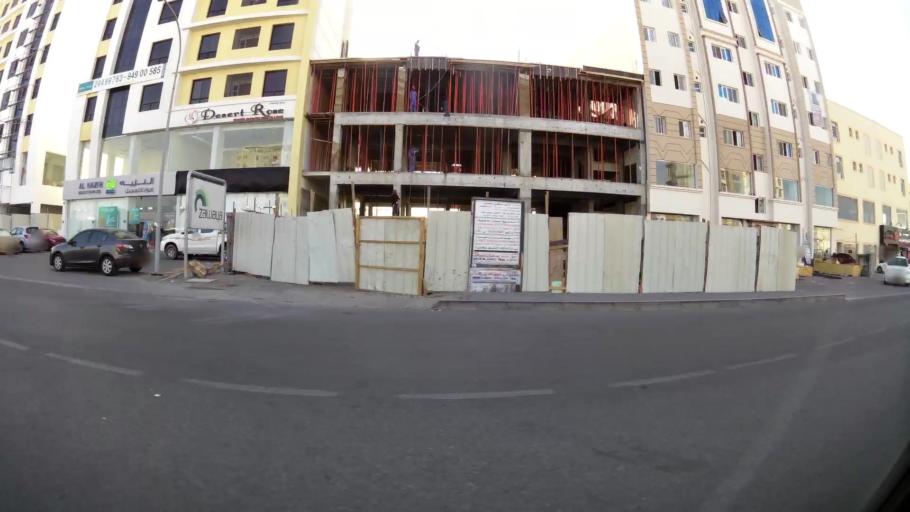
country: OM
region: Muhafazat Masqat
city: As Sib al Jadidah
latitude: 23.6267
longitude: 58.1951
